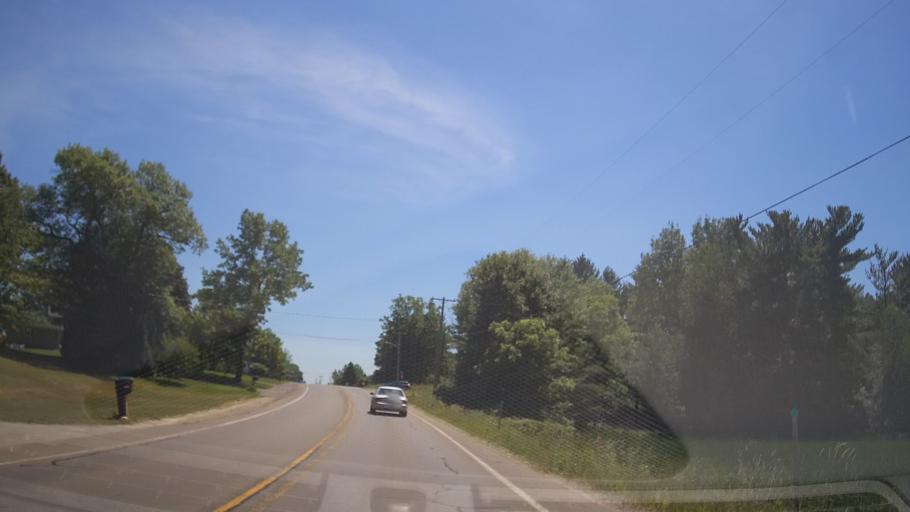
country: US
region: Michigan
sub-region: Grand Traverse County
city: Traverse City
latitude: 44.7063
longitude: -85.6926
